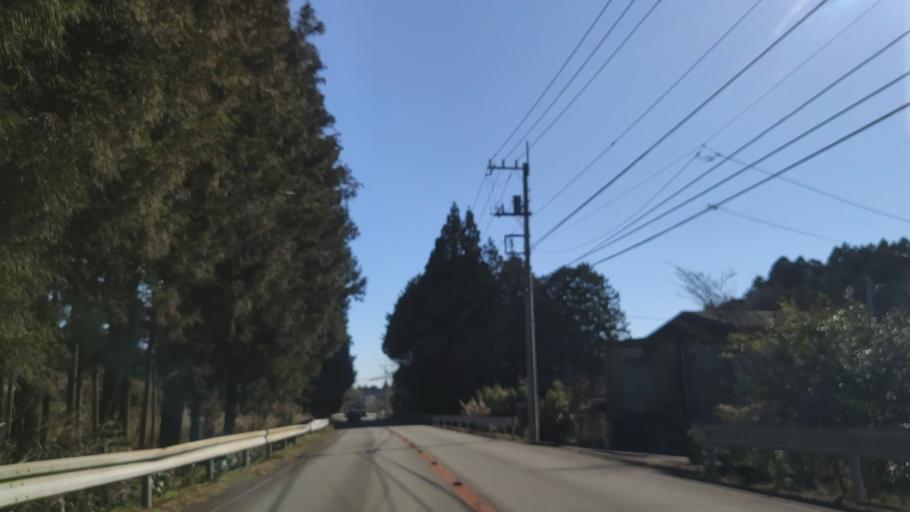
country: JP
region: Shizuoka
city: Fujinomiya
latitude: 35.3217
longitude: 138.5859
